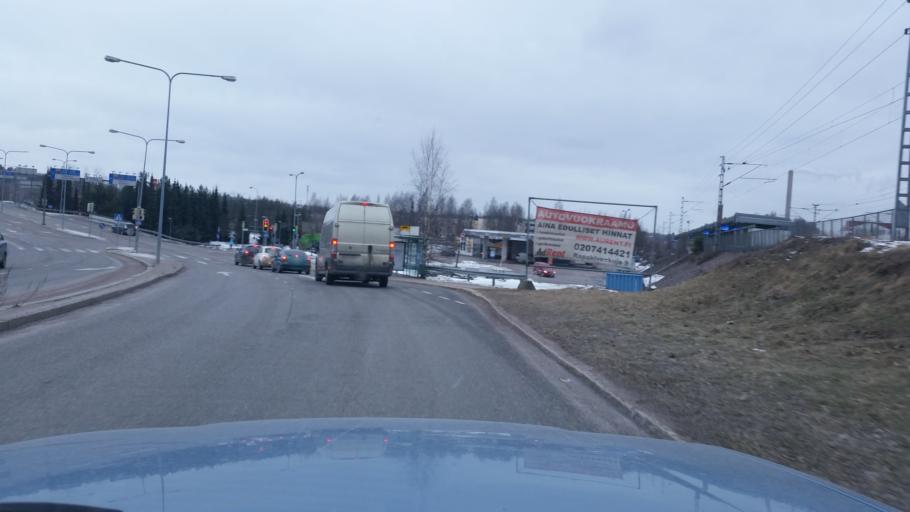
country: FI
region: Uusimaa
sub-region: Helsinki
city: Vantaa
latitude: 60.2436
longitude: 24.9967
